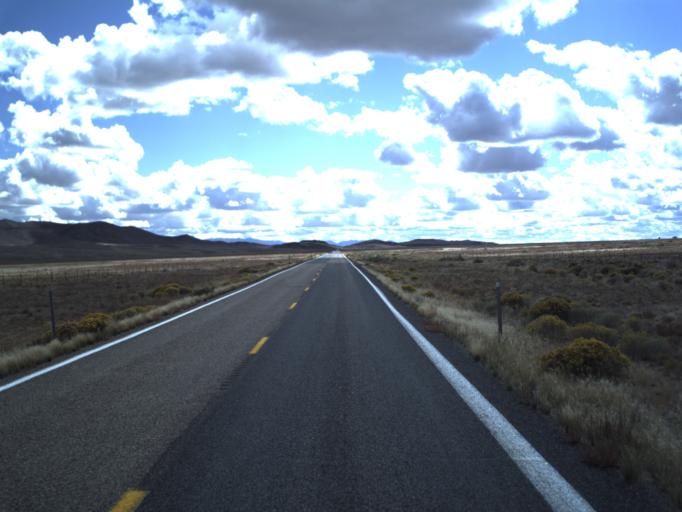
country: US
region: Utah
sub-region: Beaver County
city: Milford
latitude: 38.6709
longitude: -113.8849
